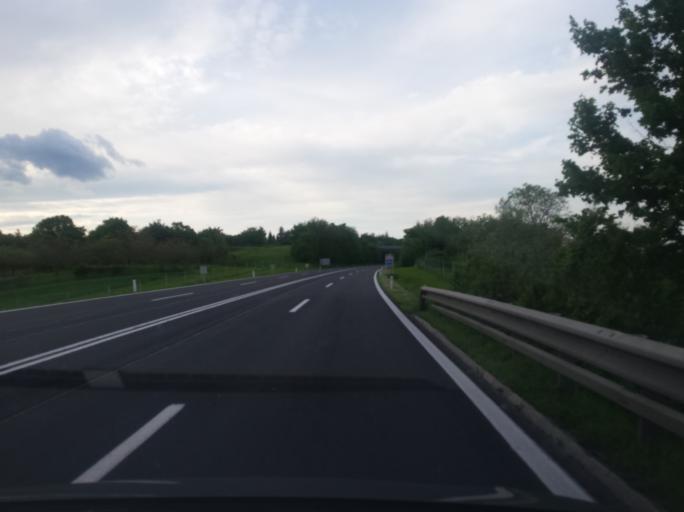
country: AT
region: Burgenland
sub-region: Politischer Bezirk Mattersburg
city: Mattersburg
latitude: 47.7277
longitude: 16.3740
